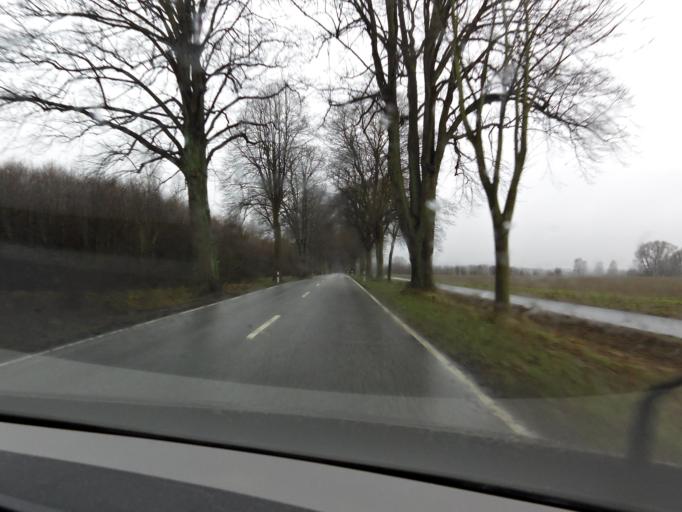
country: DE
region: Schleswig-Holstein
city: Salem
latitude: 53.6931
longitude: 10.8492
